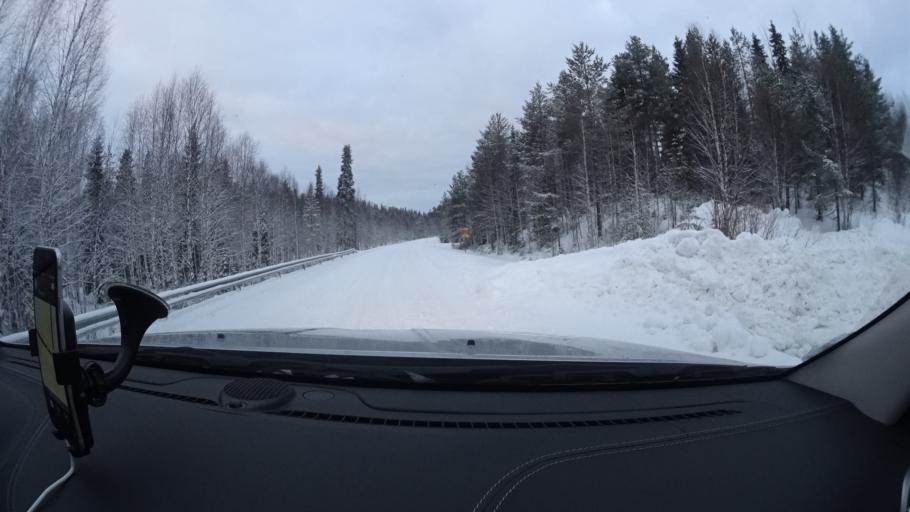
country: FI
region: Lapland
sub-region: Rovaniemi
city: Ranua
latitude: 66.3641
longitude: 26.6847
